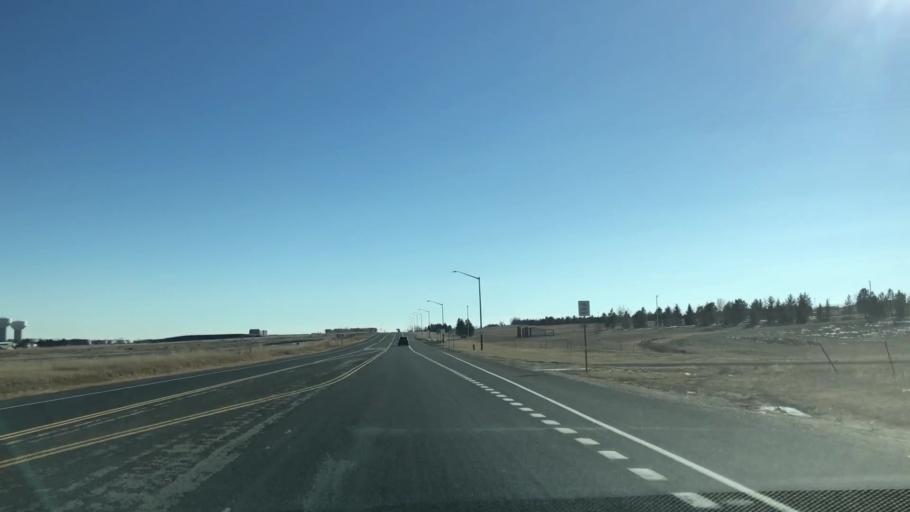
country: US
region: Colorado
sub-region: Weld County
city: Windsor
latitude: 40.4501
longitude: -104.9824
